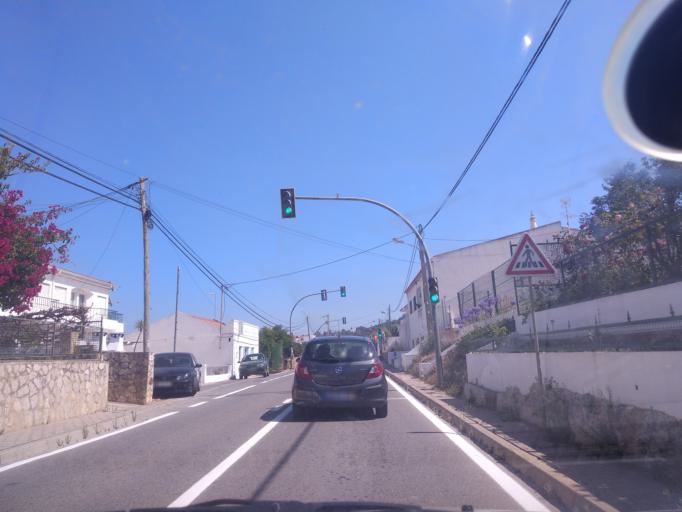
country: PT
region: Faro
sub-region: Lagos
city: Lagos
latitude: 37.1242
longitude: -8.6948
